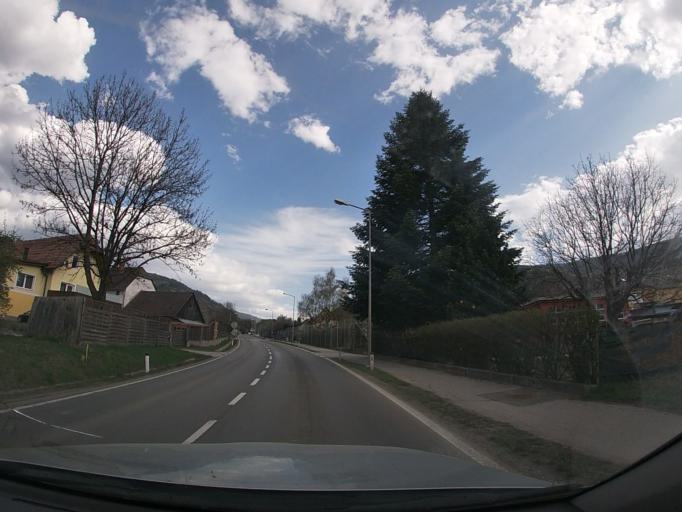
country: AT
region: Styria
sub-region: Politischer Bezirk Murau
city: Sankt Lorenzen bei Scheifling
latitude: 47.1497
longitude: 14.4126
